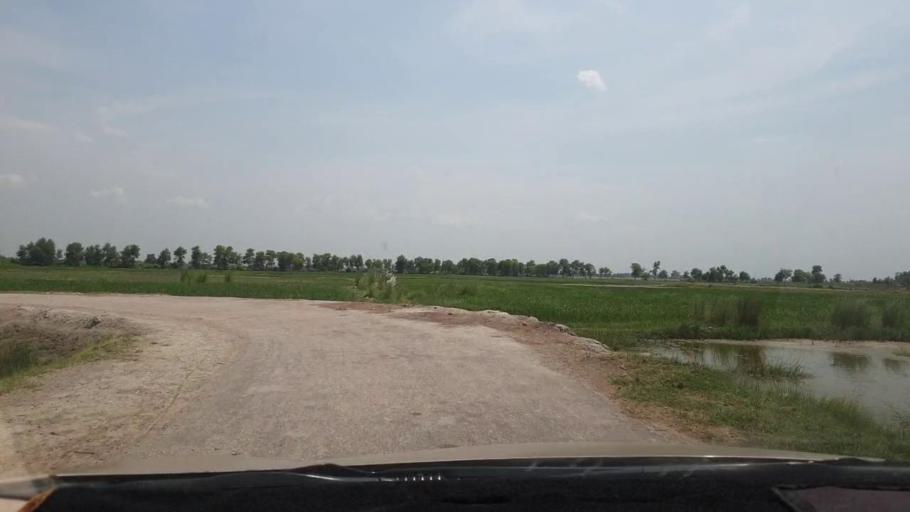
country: PK
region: Sindh
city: Naudero
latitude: 27.7333
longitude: 68.3325
